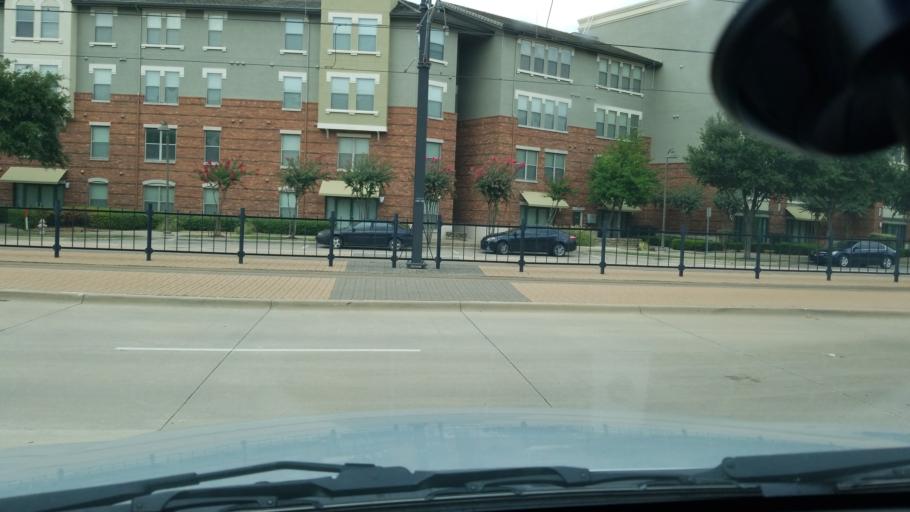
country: US
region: Texas
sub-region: Dallas County
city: Irving
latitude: 32.8628
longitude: -96.9282
